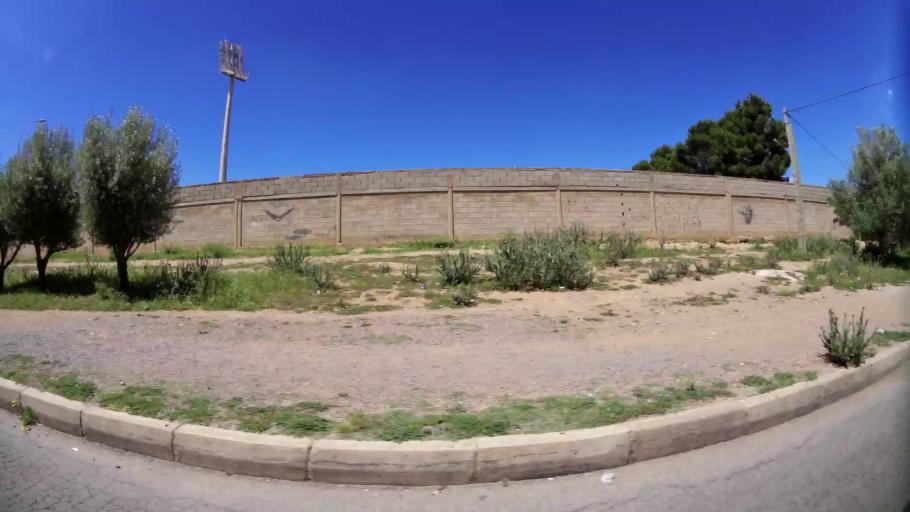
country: MA
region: Oriental
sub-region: Oujda-Angad
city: Oujda
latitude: 34.6609
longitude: -1.9338
